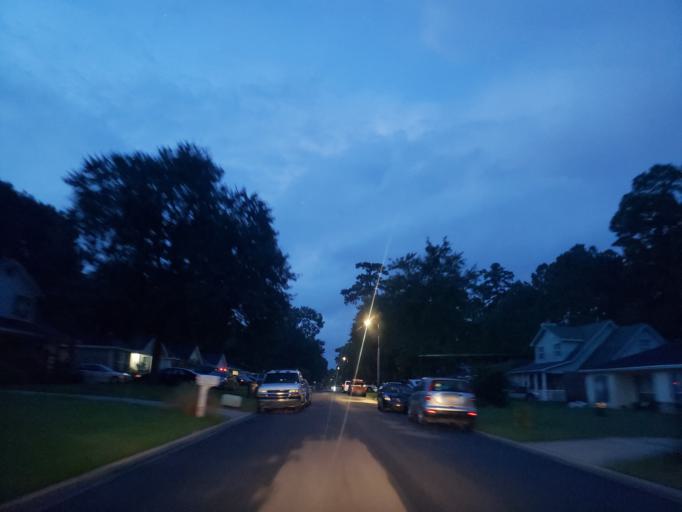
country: US
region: Georgia
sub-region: Chatham County
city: Isle of Hope
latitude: 31.9961
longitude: -81.0746
